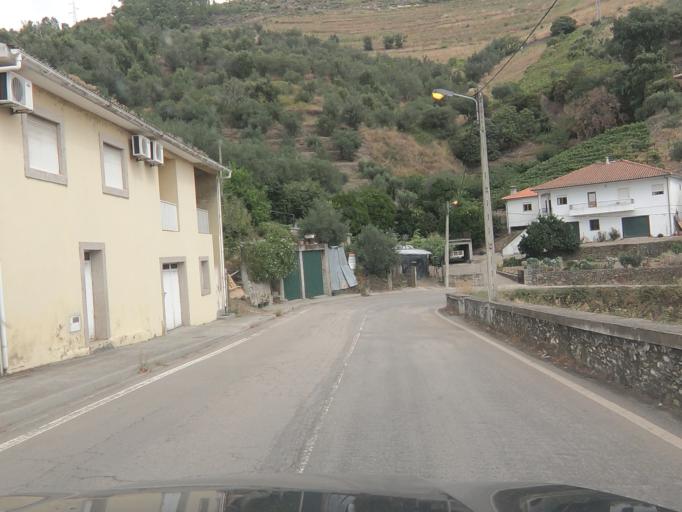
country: PT
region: Vila Real
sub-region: Santa Marta de Penaguiao
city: Santa Marta de Penaguiao
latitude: 41.2400
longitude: -7.7664
